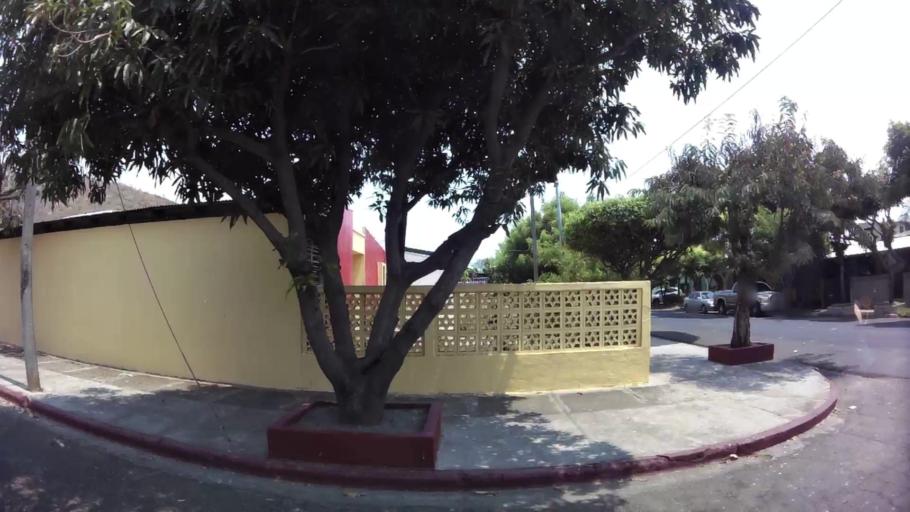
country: NI
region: Managua
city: Ciudad Sandino
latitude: 12.1517
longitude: -86.3144
